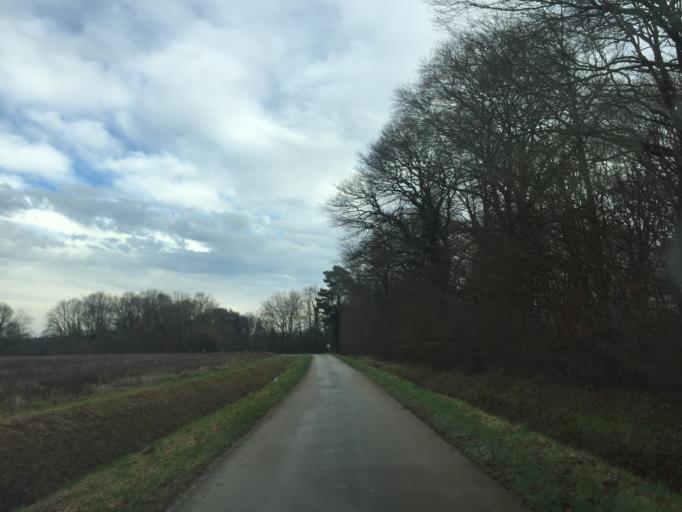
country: FR
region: Franche-Comte
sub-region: Departement du Jura
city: Chaussin
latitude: 46.9081
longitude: 5.4644
